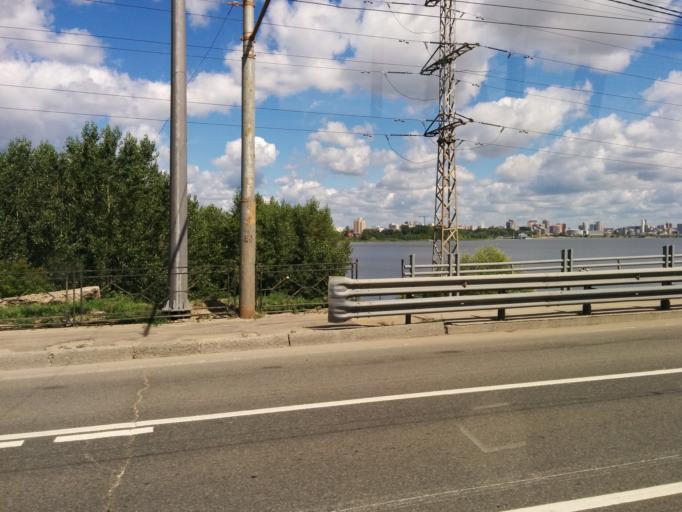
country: RU
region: Tatarstan
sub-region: Gorod Kazan'
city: Kazan
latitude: 55.7983
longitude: 49.0771
